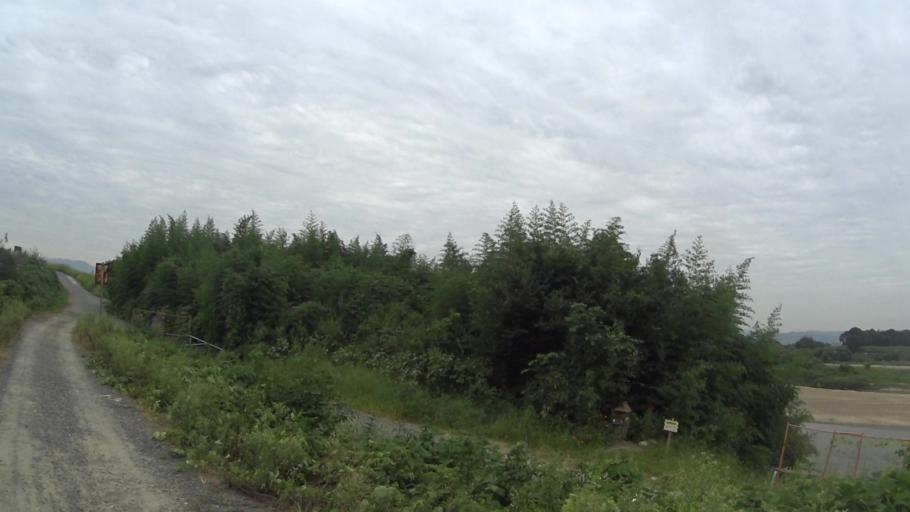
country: JP
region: Kyoto
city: Uji
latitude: 34.8643
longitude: 135.7767
